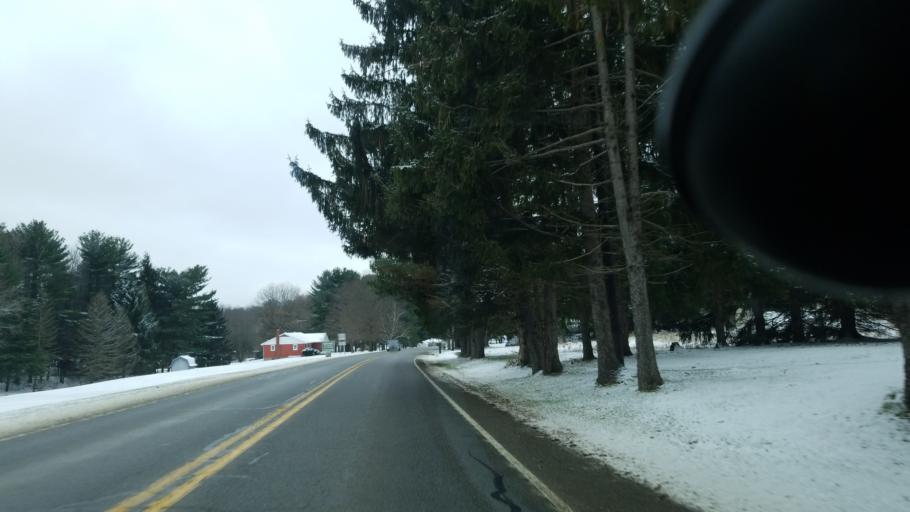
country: US
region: Pennsylvania
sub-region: Jefferson County
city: Albion
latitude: 40.9319
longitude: -78.9071
